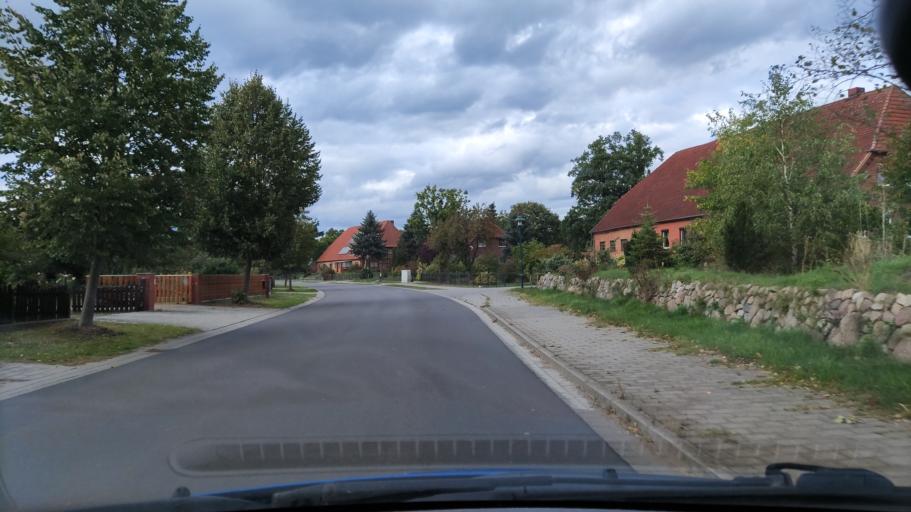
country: DE
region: Lower Saxony
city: Neu Darchau
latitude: 53.2296
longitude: 10.9834
